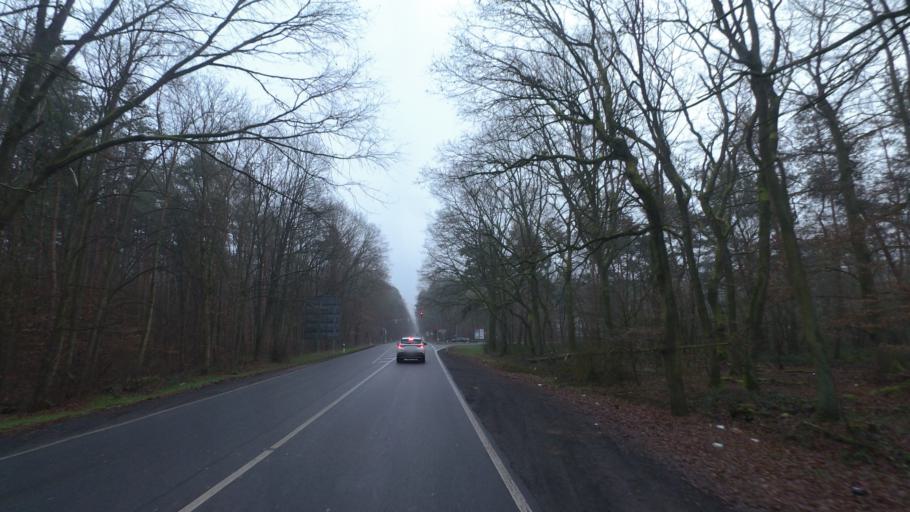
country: DE
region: Hesse
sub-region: Regierungsbezirk Darmstadt
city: Rodgau
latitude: 50.0608
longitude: 8.8976
